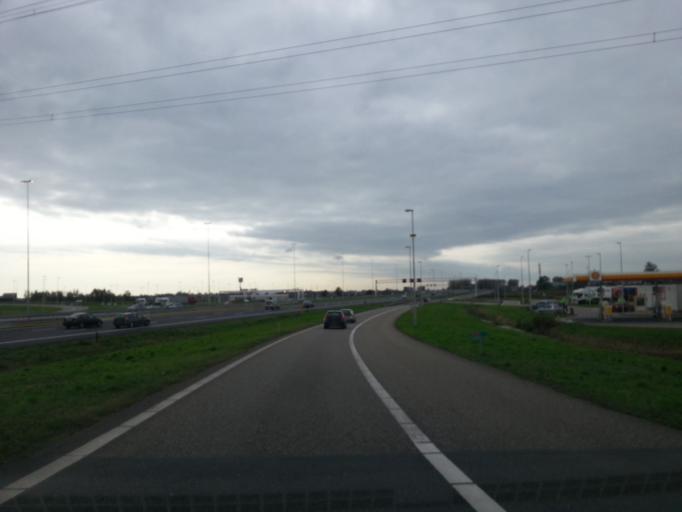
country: NL
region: South Holland
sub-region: Gemeente Leiderdorp
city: Leiderdorp
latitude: 52.1631
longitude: 4.5564
